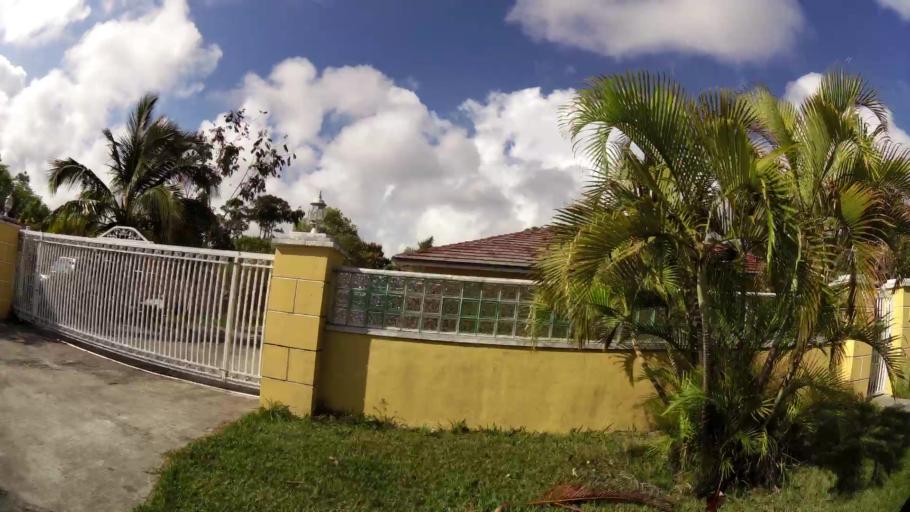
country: BS
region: Freeport
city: Lucaya
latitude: 26.5260
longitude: -78.6796
